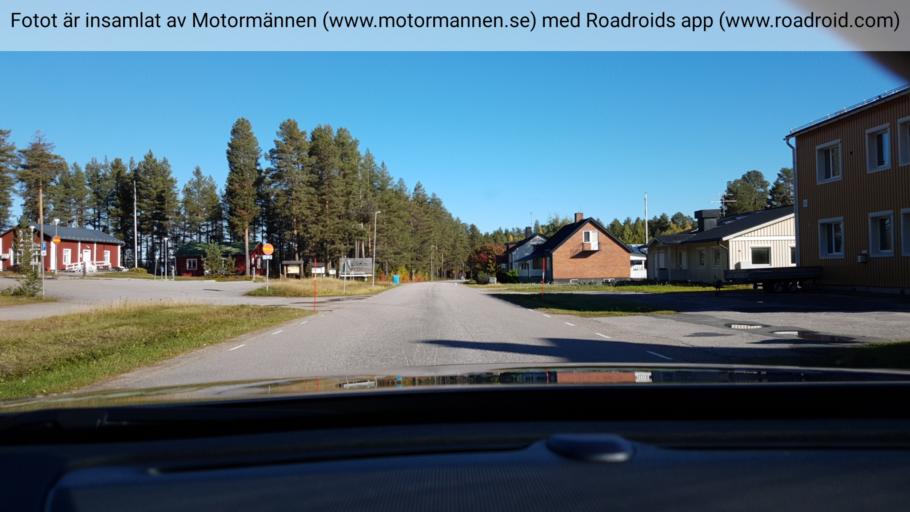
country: SE
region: Norrbotten
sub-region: Gallivare Kommun
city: Gaellivare
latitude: 66.4339
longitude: 20.6098
